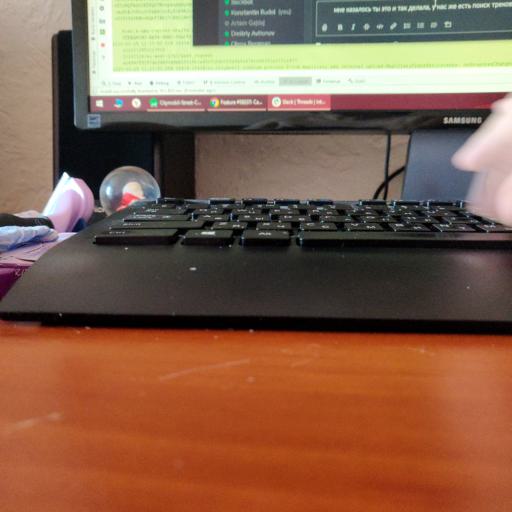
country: FI
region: Haeme
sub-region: Forssa
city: Humppila
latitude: 60.9144
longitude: 23.3738
